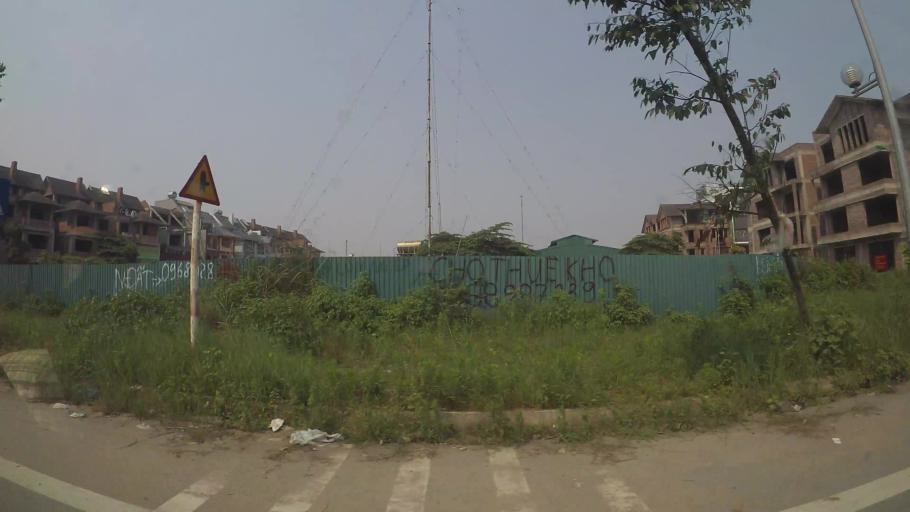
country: VN
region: Ha Noi
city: Ha Dong
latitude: 20.9667
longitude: 105.7984
